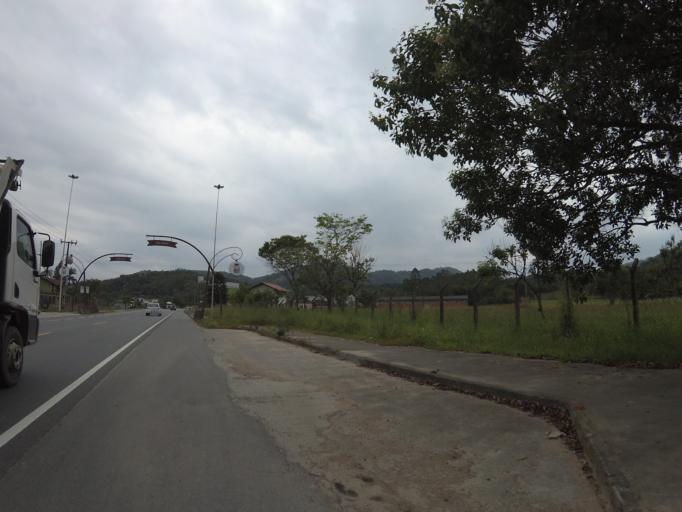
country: BR
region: Santa Catarina
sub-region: Pomerode
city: Pomerode
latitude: -26.8321
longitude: -49.1628
